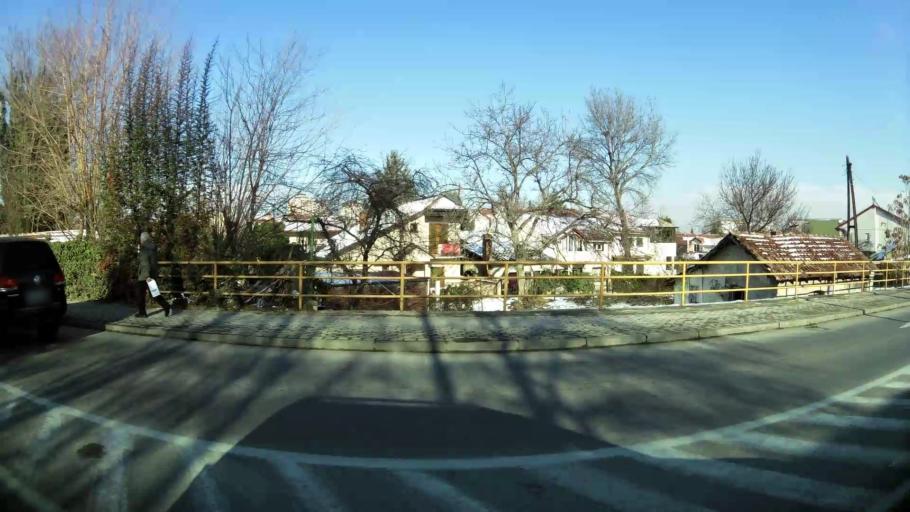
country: MK
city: Krushopek
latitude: 42.0002
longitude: 21.3791
